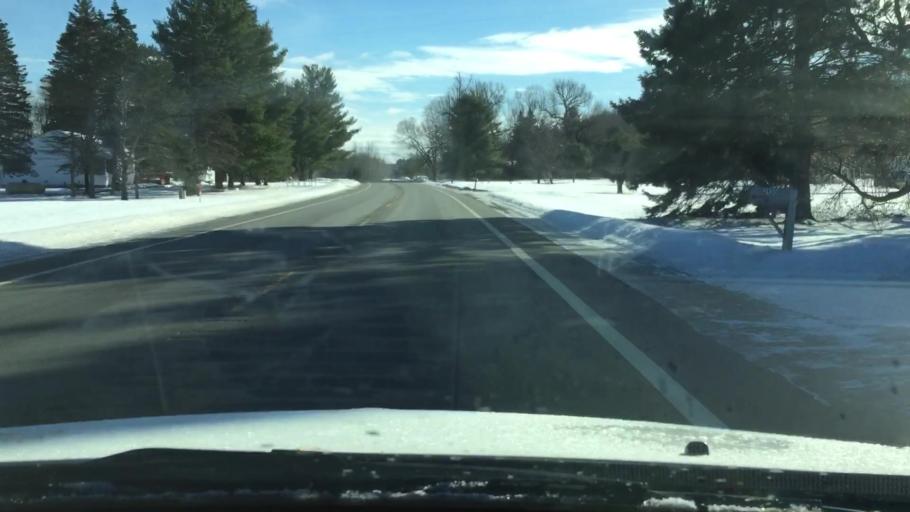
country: US
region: Michigan
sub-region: Charlevoix County
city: East Jordan
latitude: 45.0674
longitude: -85.0840
